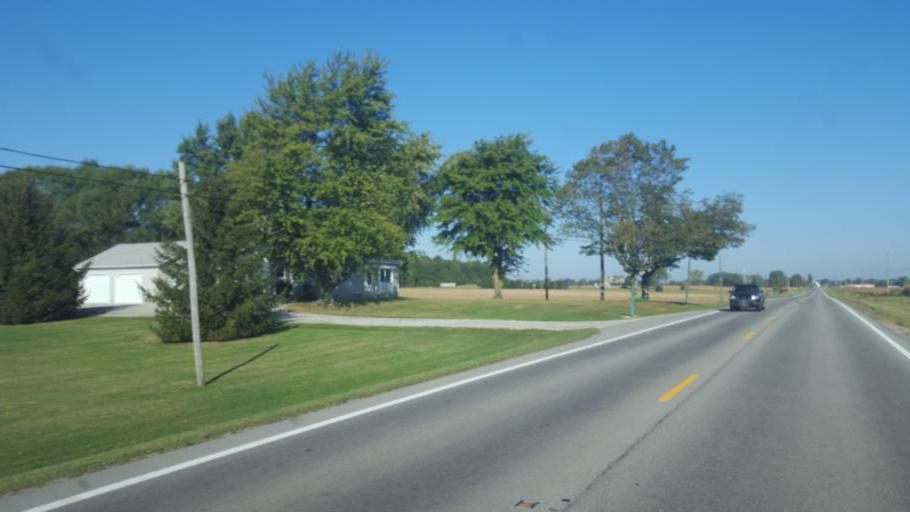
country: US
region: Ohio
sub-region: Hardin County
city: Kenton
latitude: 40.5176
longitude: -83.5080
